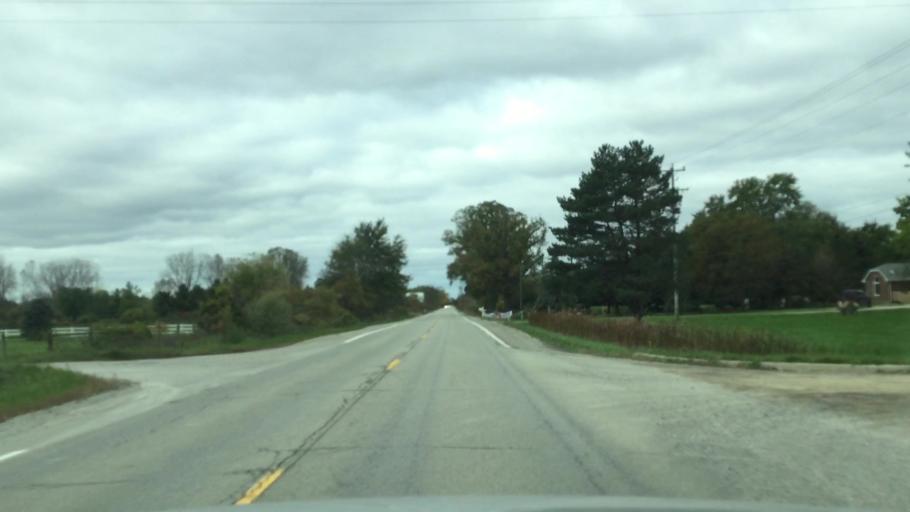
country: US
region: Michigan
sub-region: Macomb County
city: Armada
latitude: 42.8062
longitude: -82.8953
